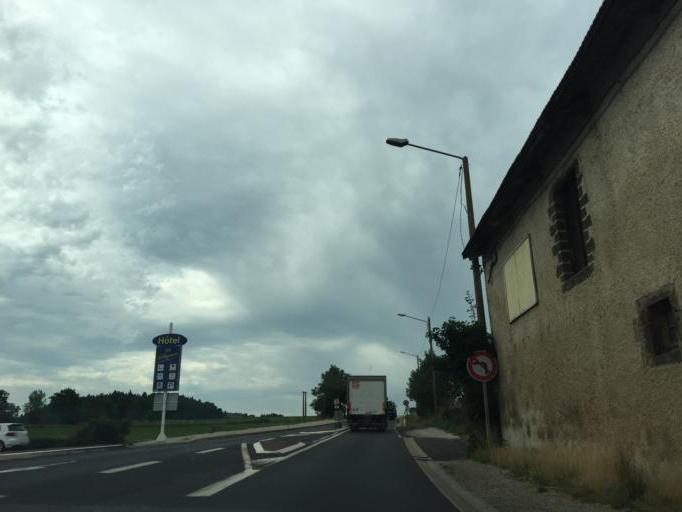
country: FR
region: Auvergne
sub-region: Departement de la Haute-Loire
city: Solignac-sur-Loire
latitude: 44.9444
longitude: 3.8480
